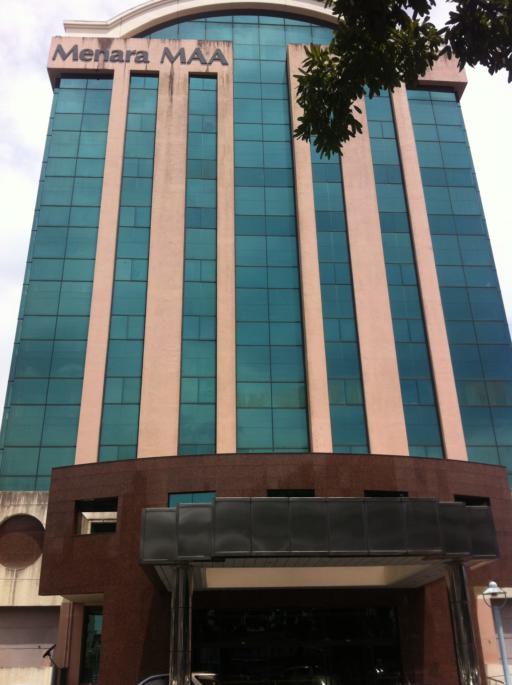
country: MY
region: Sarawak
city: Kuching
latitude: 1.5523
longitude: 110.3567
